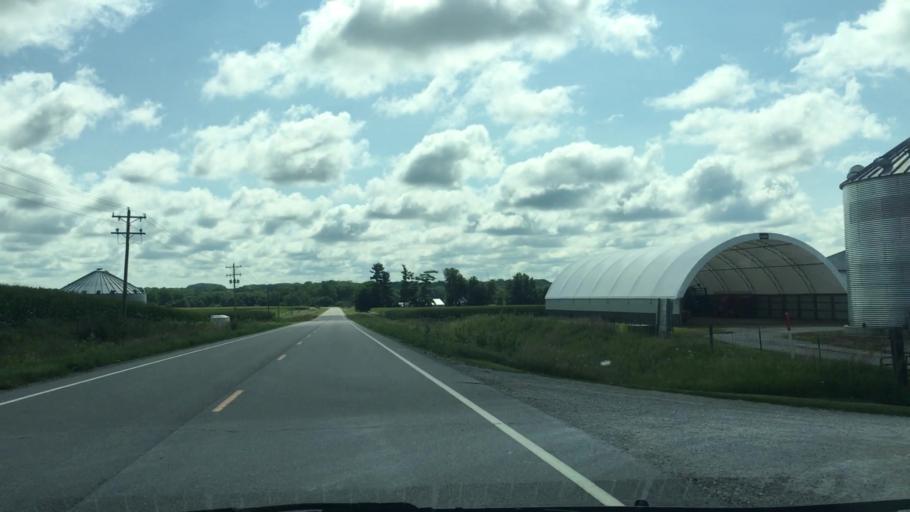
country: US
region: Iowa
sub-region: Linn County
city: Mount Vernon
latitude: 41.8418
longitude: -91.4081
